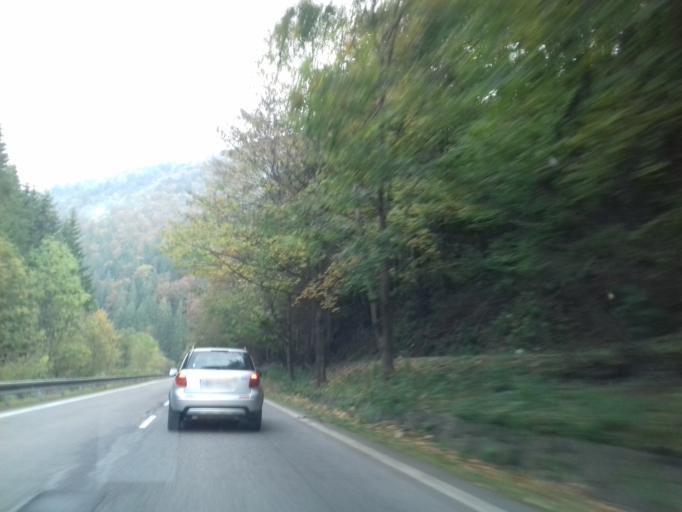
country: SK
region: Zilinsky
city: Ruzomberok
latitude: 48.9015
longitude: 19.2678
